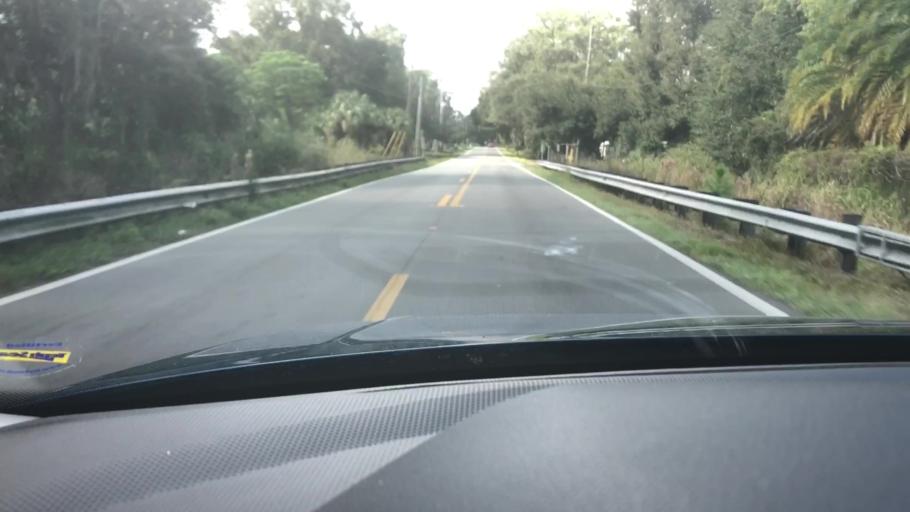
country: US
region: Florida
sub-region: Polk County
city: Winston
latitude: 28.0333
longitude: -82.0077
